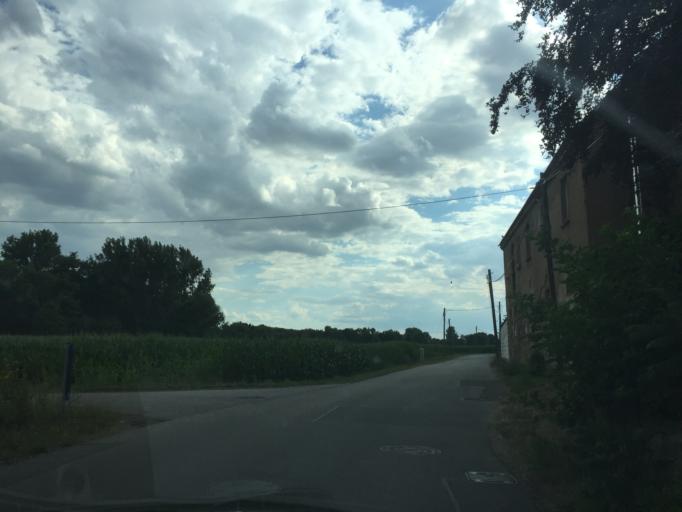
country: DE
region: Thuringia
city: Nobitz
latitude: 50.9652
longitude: 12.4587
